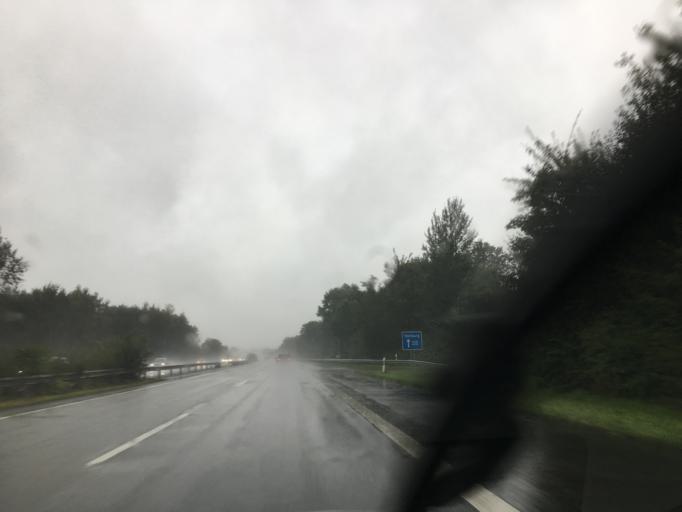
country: DE
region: Schleswig-Holstein
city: Rumohr
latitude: 54.2437
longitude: 10.0224
